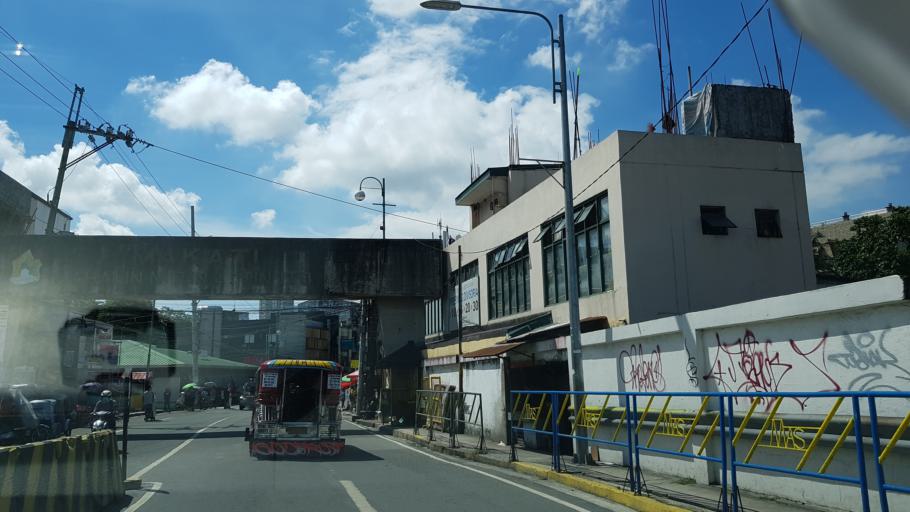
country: PH
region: Calabarzon
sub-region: Province of Rizal
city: Pateros
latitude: 14.5458
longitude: 121.0652
